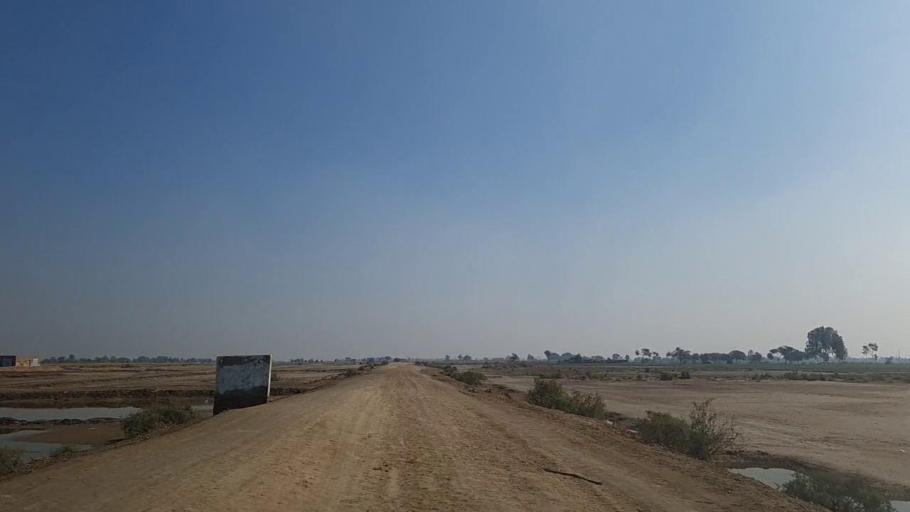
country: PK
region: Sindh
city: Daur
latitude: 26.4663
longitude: 68.3223
